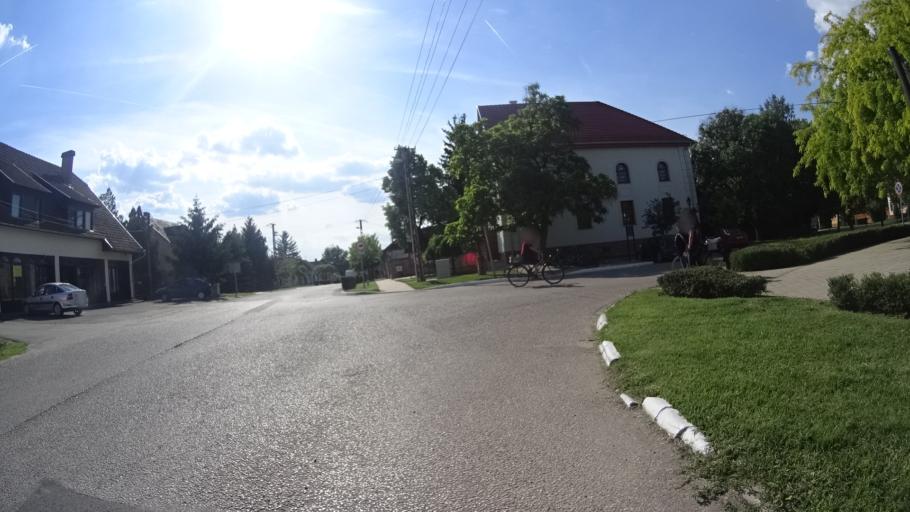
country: HU
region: Bacs-Kiskun
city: Tiszakecske
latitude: 46.9299
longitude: 20.1020
